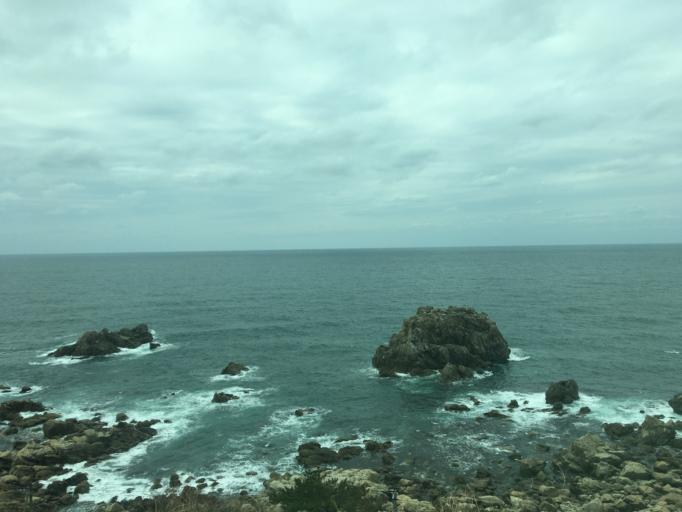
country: JP
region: Akita
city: Noshiromachi
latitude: 40.4406
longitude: 139.9409
